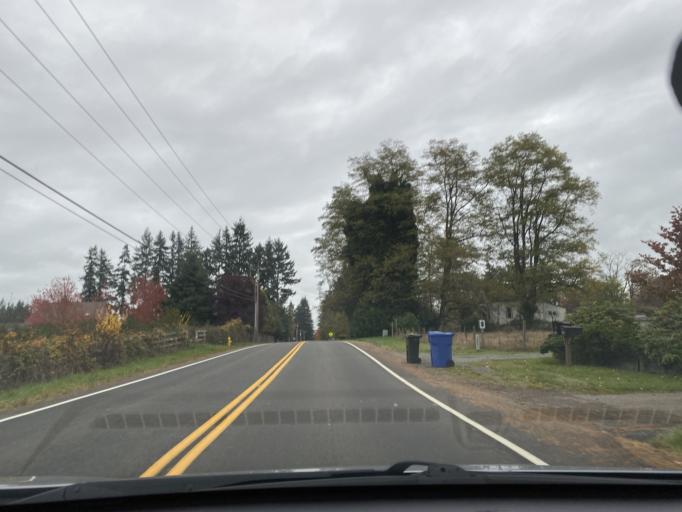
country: US
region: Washington
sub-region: King County
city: Lake Morton-Berrydale
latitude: 47.3005
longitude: -122.1295
